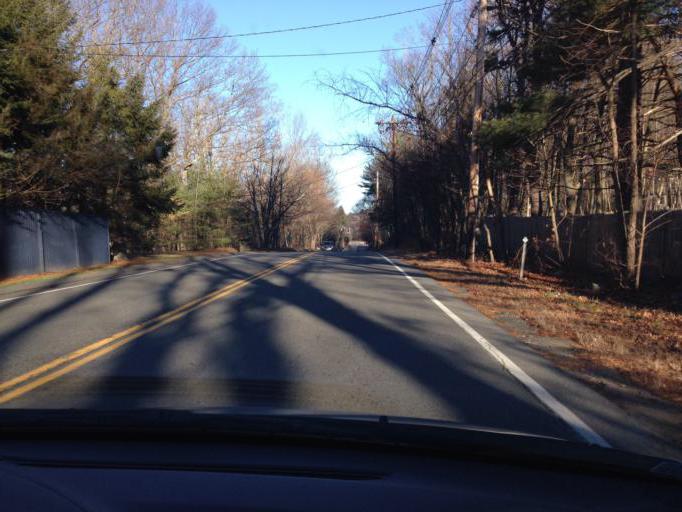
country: US
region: Massachusetts
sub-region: Middlesex County
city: Bedford
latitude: 42.5146
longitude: -71.2843
